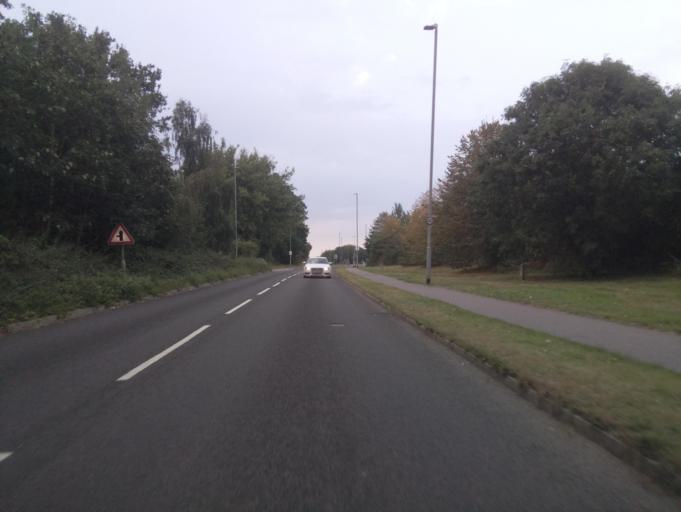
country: GB
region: England
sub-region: Nottinghamshire
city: South Collingham
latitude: 53.1469
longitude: -0.6691
